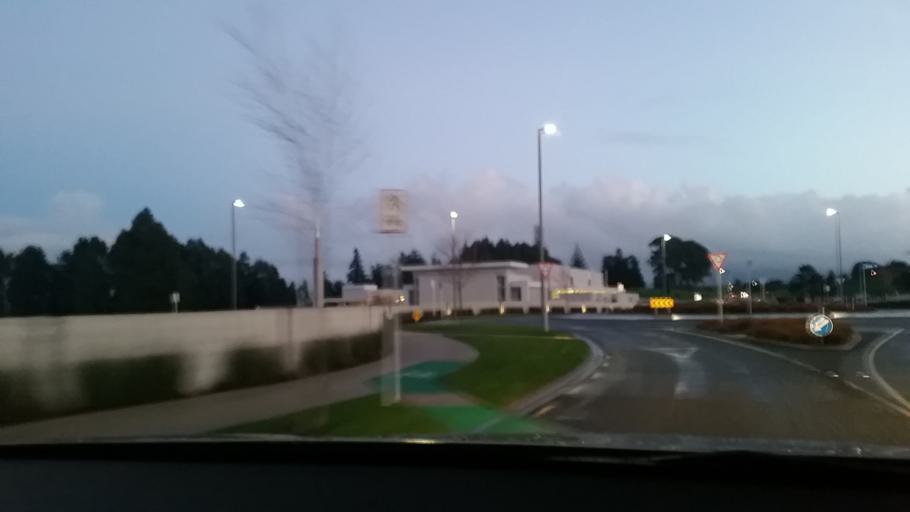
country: NZ
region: Waikato
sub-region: Hamilton City
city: Hamilton
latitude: -37.8217
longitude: 175.2264
